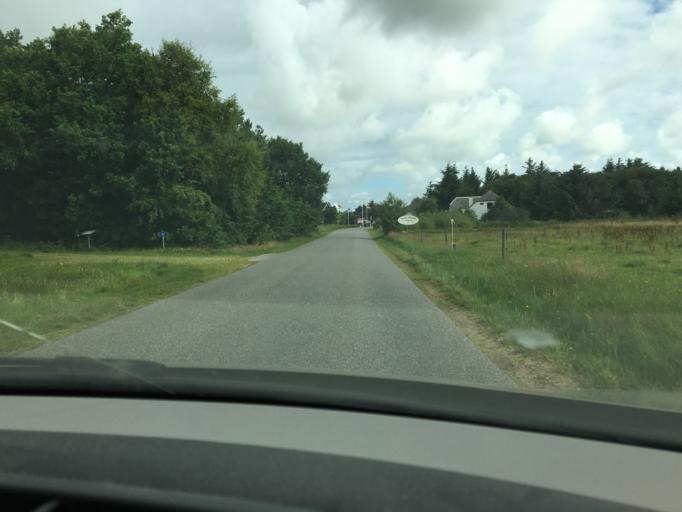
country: DK
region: Central Jutland
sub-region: Ringkobing-Skjern Kommune
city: Hvide Sande
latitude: 55.8252
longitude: 8.2157
